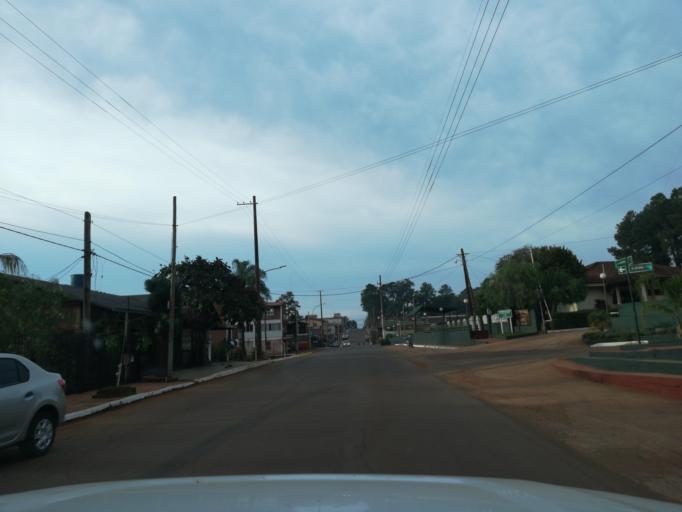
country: AR
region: Misiones
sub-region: Departamento de San Pedro
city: San Pedro
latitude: -26.6230
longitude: -54.1161
